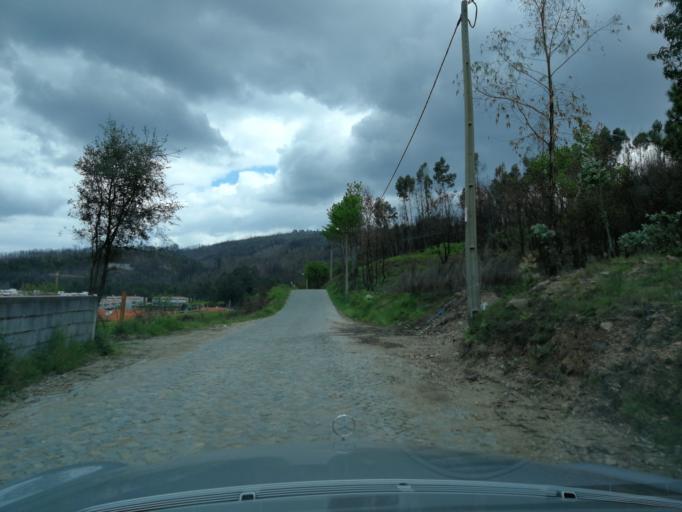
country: PT
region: Braga
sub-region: Braga
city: Braga
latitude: 41.5239
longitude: -8.3979
